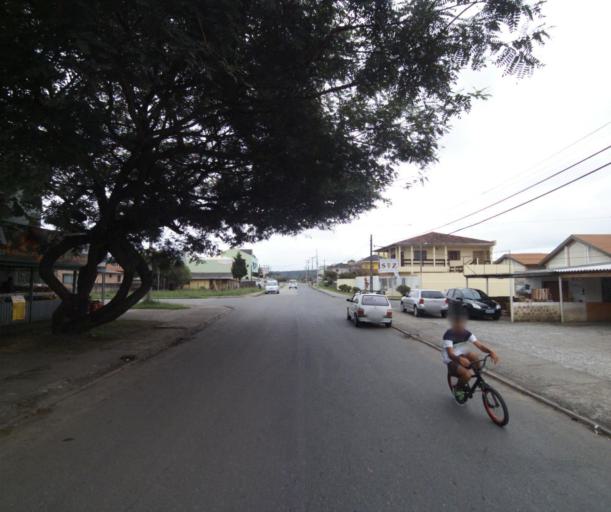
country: BR
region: Parana
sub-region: Quatro Barras
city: Quatro Barras
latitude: -25.3628
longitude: -49.1022
